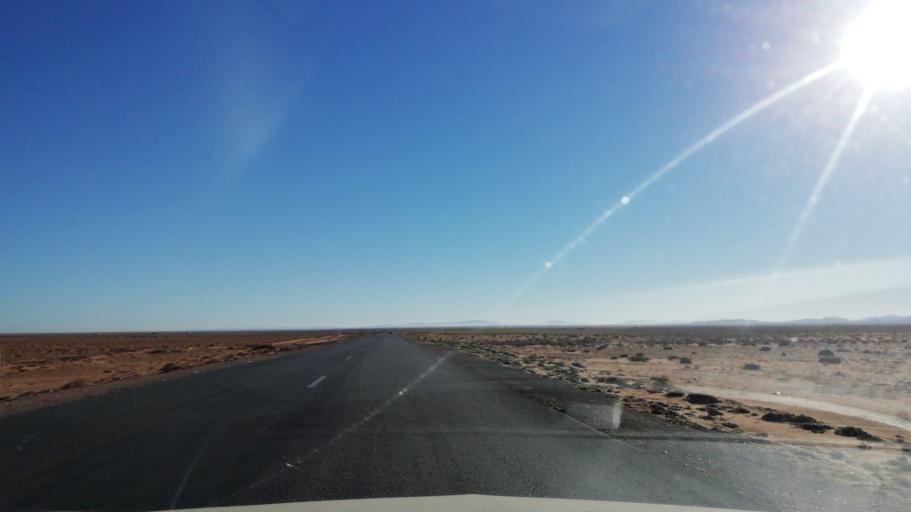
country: DZ
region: El Bayadh
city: El Bayadh
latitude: 33.8602
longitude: 0.5558
